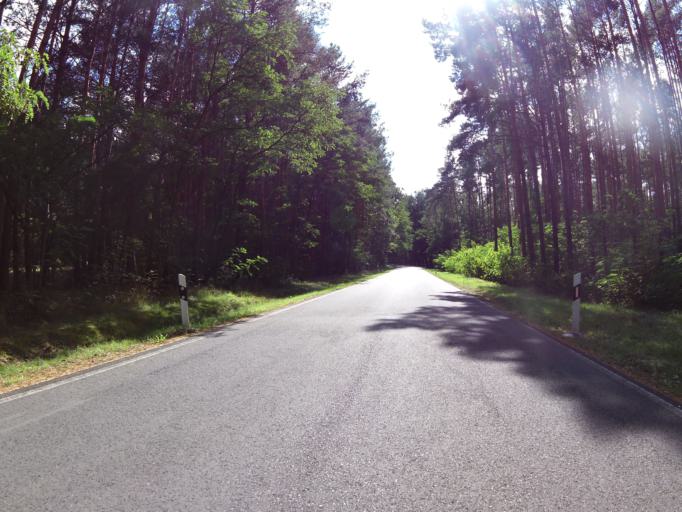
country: DE
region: Brandenburg
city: Munchehofe
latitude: 52.2025
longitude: 13.8575
